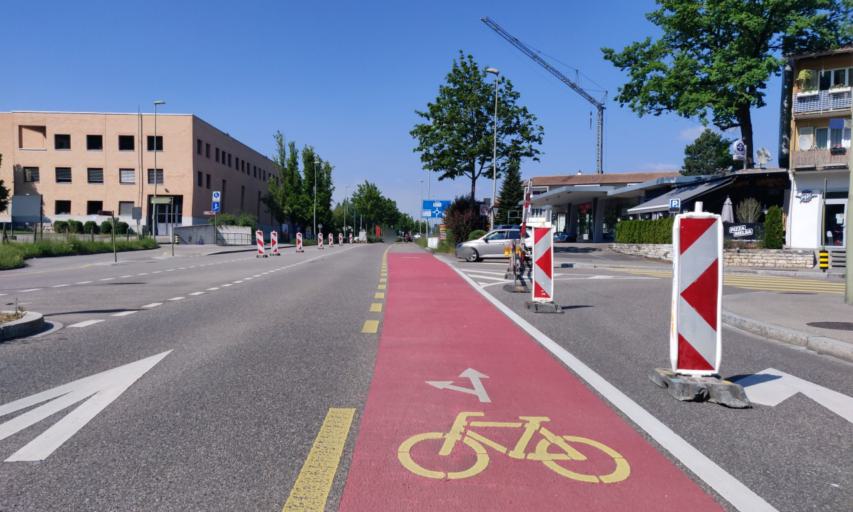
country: CH
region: Basel-Landschaft
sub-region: Bezirk Arlesheim
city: Munchenstein
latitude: 47.5245
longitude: 7.6042
